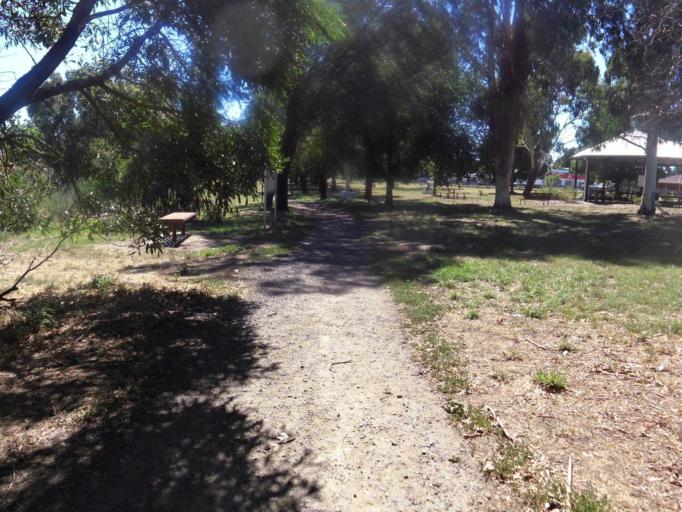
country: AU
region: Victoria
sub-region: Mount Alexander
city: Castlemaine
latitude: -37.2441
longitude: 144.4436
